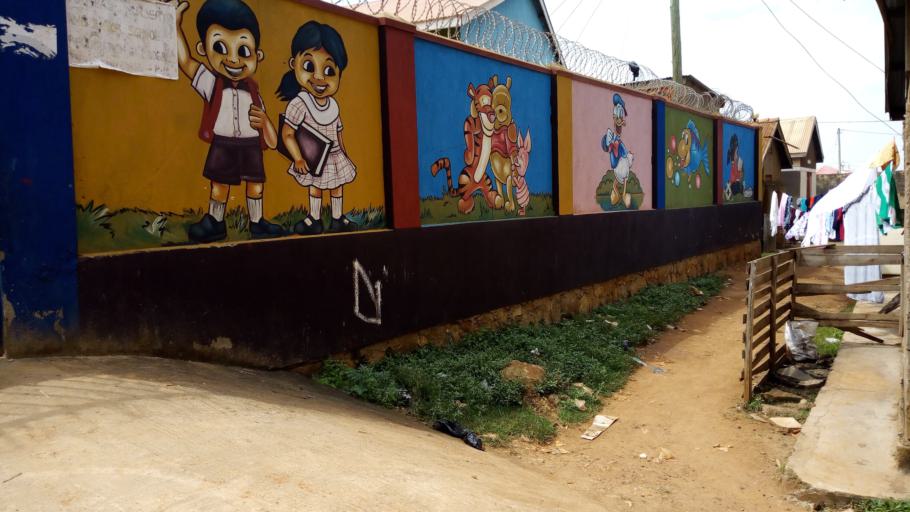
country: UG
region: Central Region
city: Kampala Central Division
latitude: 0.3509
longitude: 32.5613
